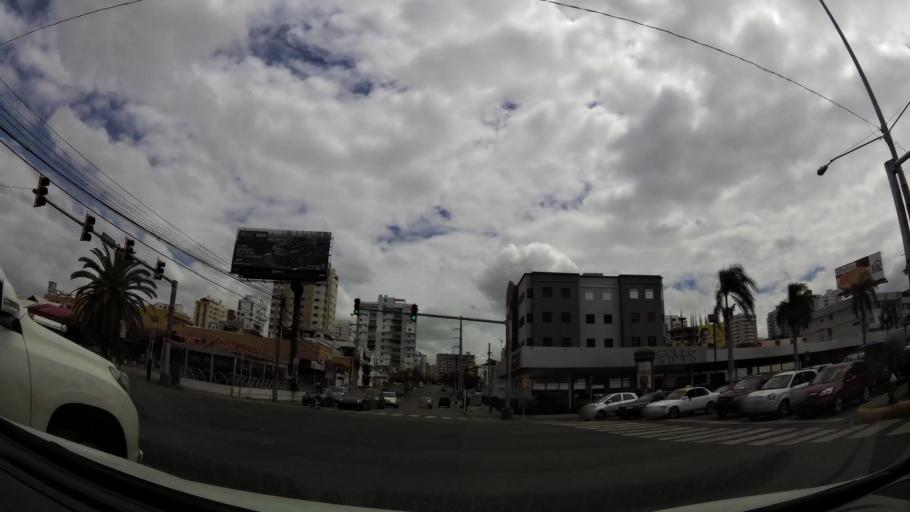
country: DO
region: Nacional
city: La Julia
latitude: 18.4787
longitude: -69.9452
